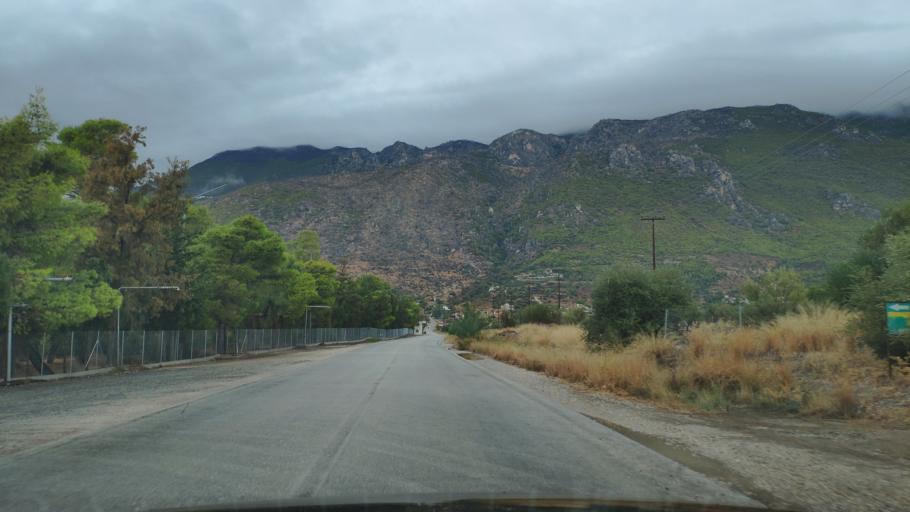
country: GR
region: Peloponnese
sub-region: Nomos Korinthias
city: Loutraki
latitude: 37.9713
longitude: 22.9874
